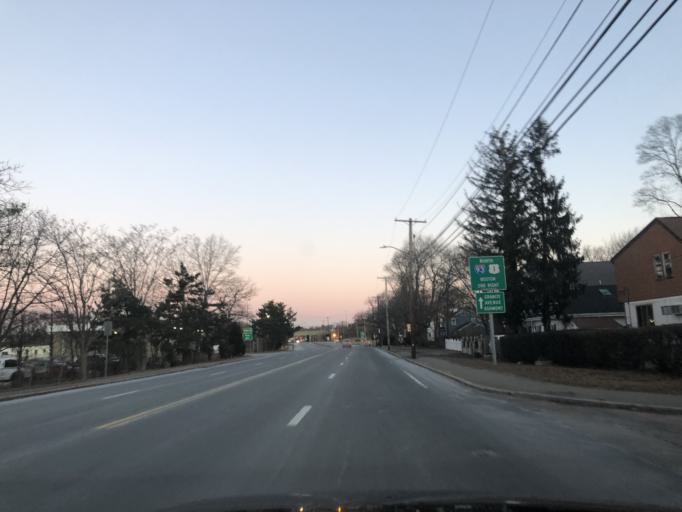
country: US
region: Massachusetts
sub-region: Norfolk County
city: Milton
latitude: 42.2714
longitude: -71.0478
